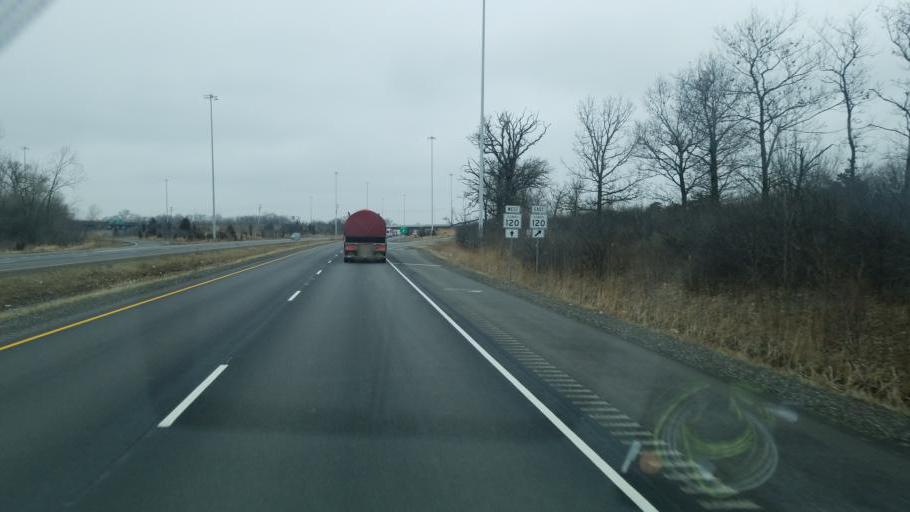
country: US
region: Illinois
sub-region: Lake County
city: Park City
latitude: 42.3443
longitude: -87.8898
